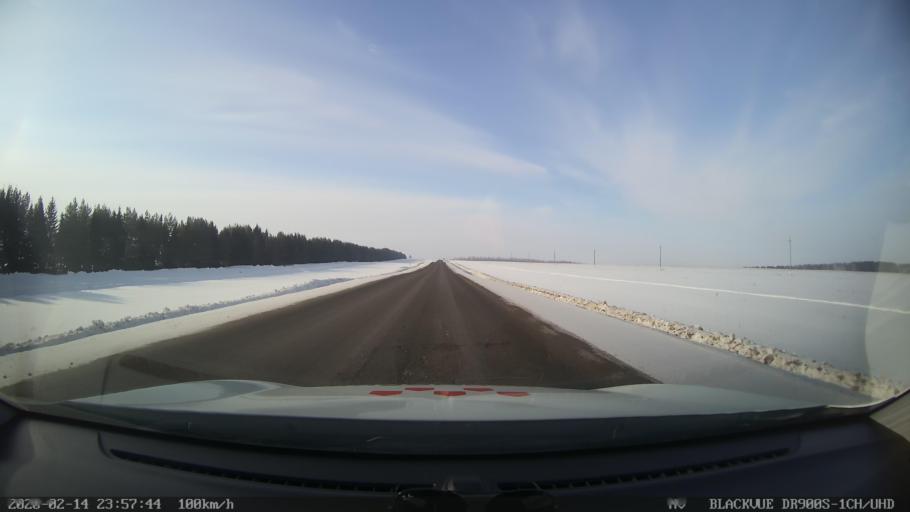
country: RU
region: Tatarstan
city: Kuybyshevskiy Zaton
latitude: 55.3359
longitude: 49.1032
